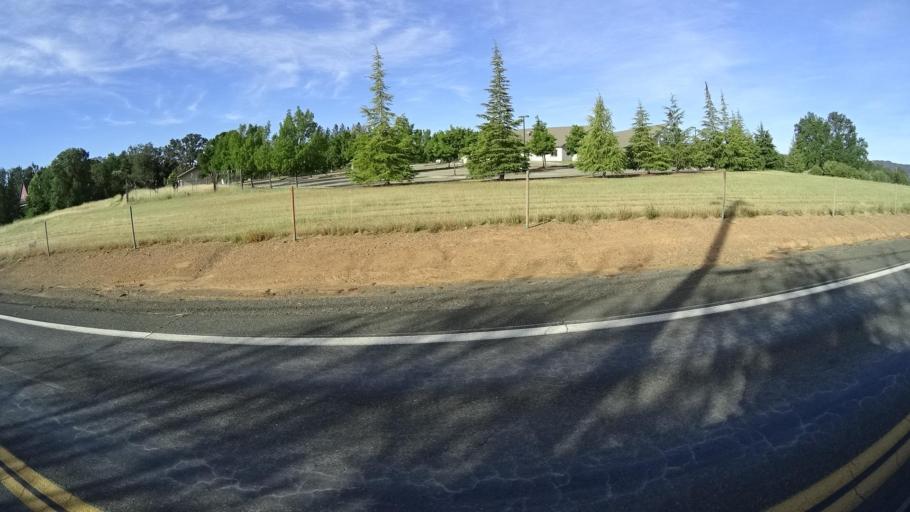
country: US
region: California
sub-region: Lake County
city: North Lakeport
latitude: 39.0826
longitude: -122.9240
